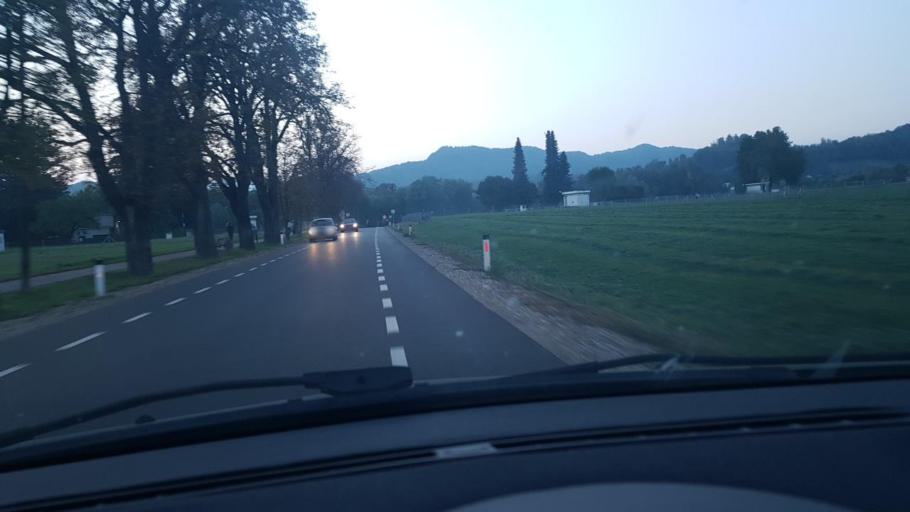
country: SI
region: Maribor
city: Kamnica
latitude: 46.5693
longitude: 15.6292
